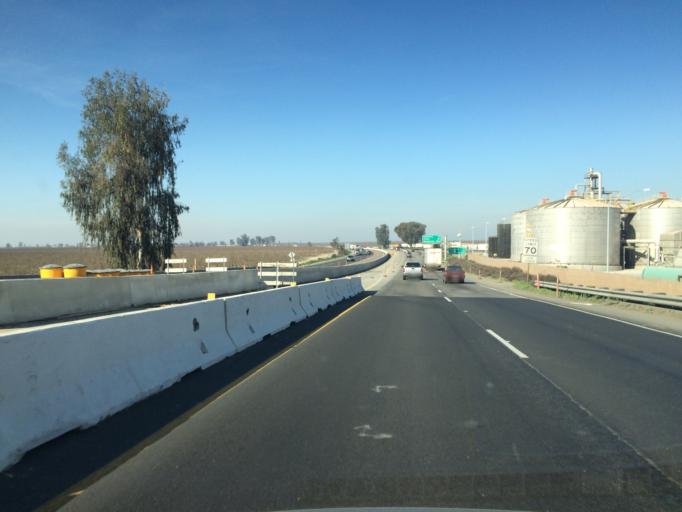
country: US
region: California
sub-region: Tulare County
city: Goshen
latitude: 36.3571
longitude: -119.4284
